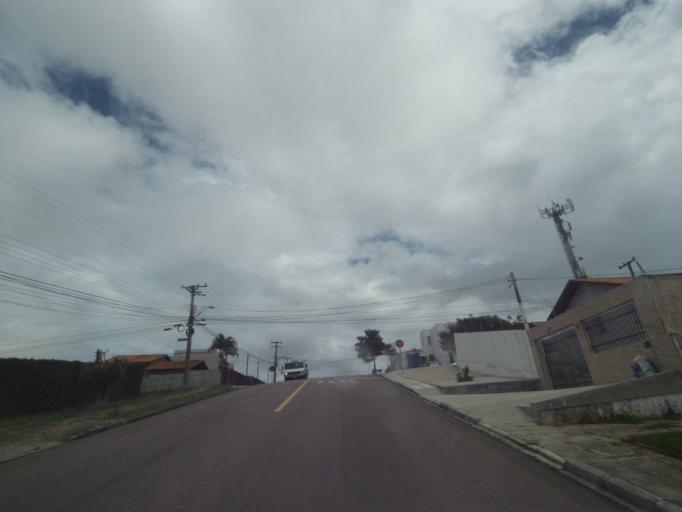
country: BR
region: Parana
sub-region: Curitiba
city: Curitiba
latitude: -25.4814
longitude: -49.2811
